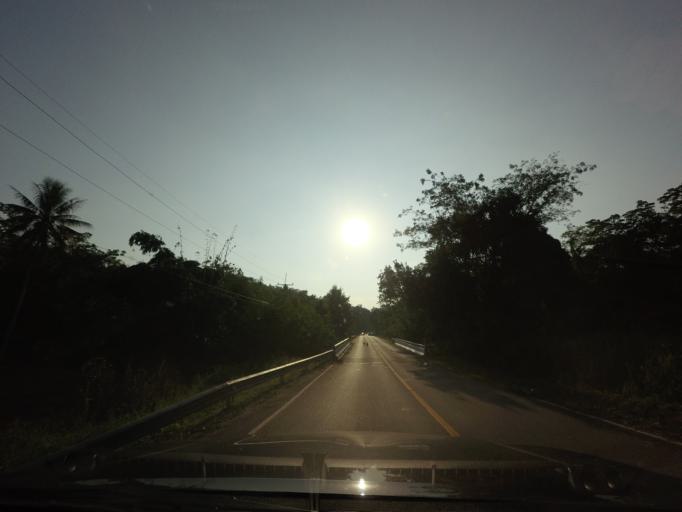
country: TH
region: Nan
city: Na Noi
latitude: 18.3358
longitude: 100.7825
